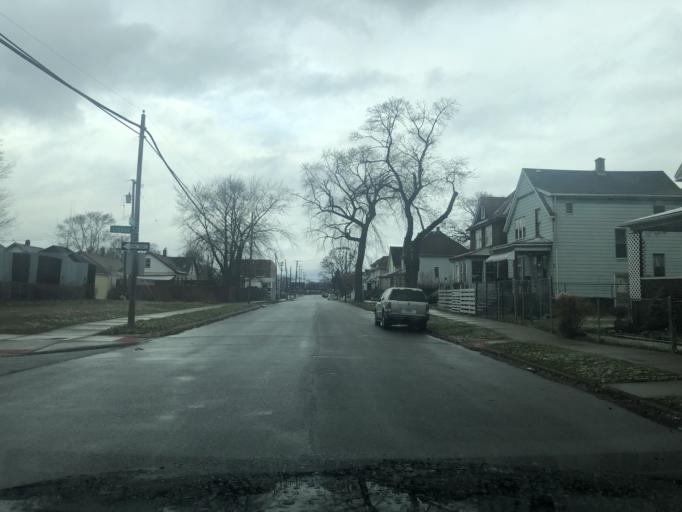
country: US
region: Michigan
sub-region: Wayne County
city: River Rouge
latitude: 42.3077
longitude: -83.1138
